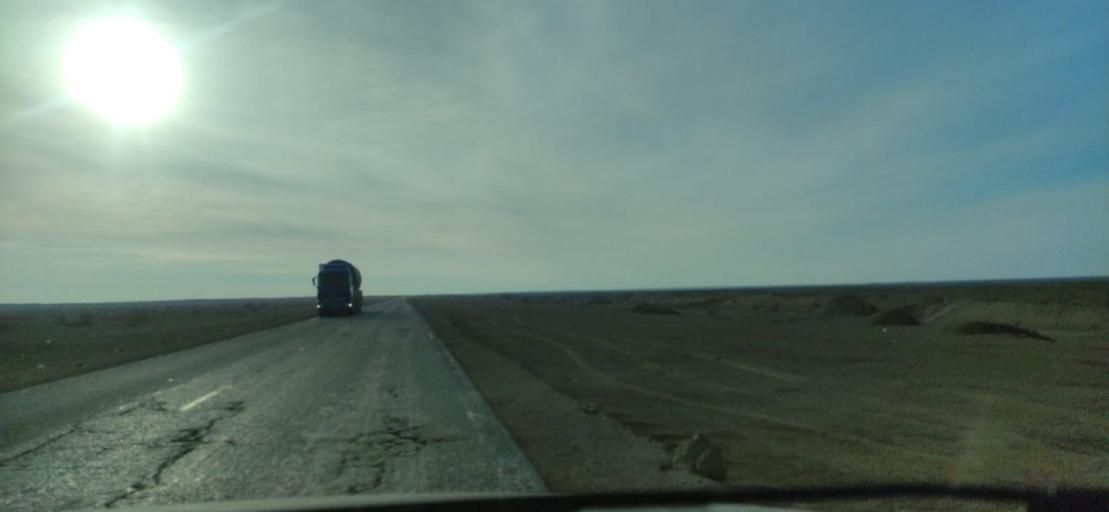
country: KZ
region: Qaraghandy
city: Saryshaghan
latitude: 46.3078
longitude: 73.7593
